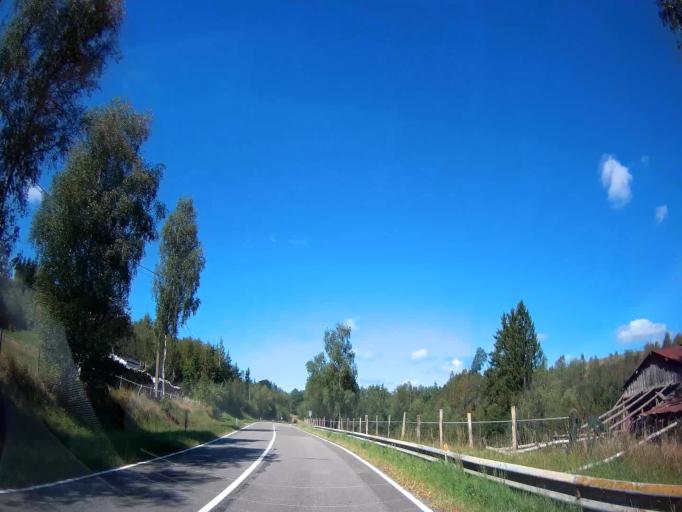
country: BE
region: Wallonia
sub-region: Province du Luxembourg
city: Bertogne
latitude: 50.1141
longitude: 5.6281
